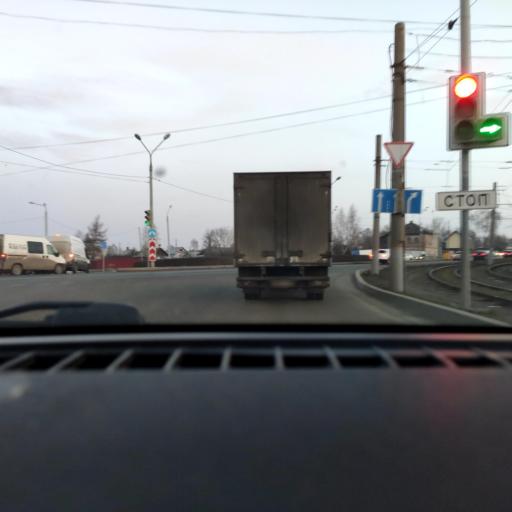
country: RU
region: Perm
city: Kondratovo
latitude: 57.9601
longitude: 56.1350
